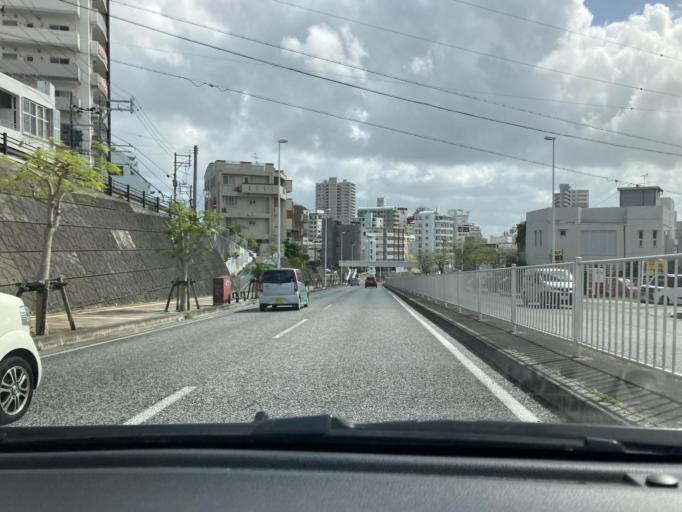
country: JP
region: Okinawa
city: Naha-shi
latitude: 26.2225
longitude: 127.6925
